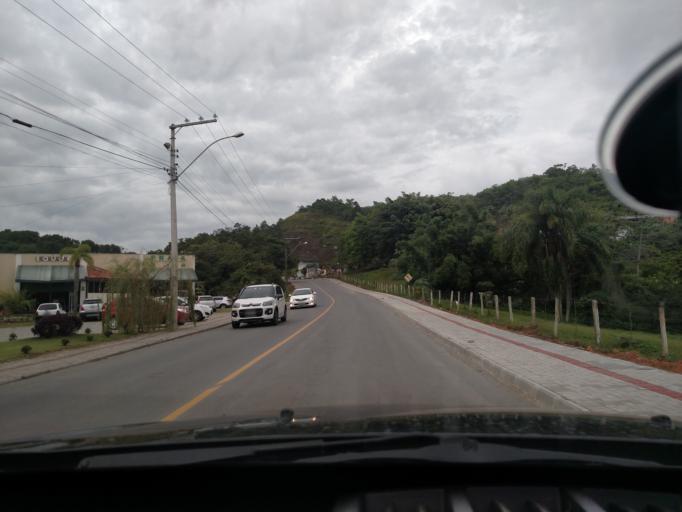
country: BR
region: Santa Catarina
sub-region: Porto Belo
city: Porto Belo
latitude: -27.1549
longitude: -48.5132
